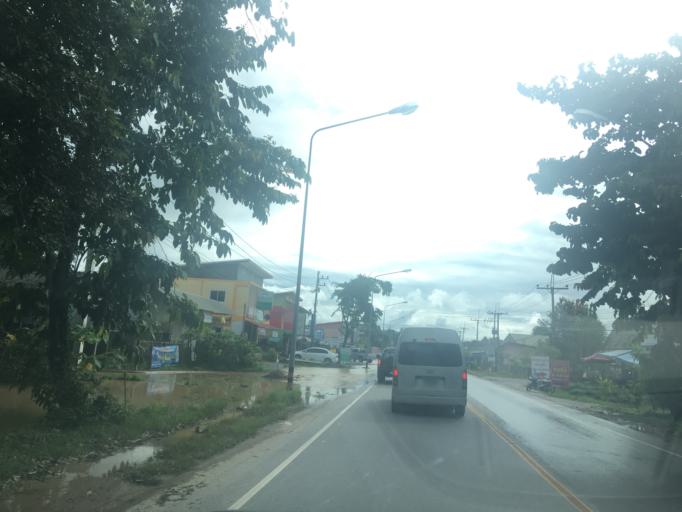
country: TH
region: Chiang Rai
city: Mae Lao
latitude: 19.8530
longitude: 99.7457
